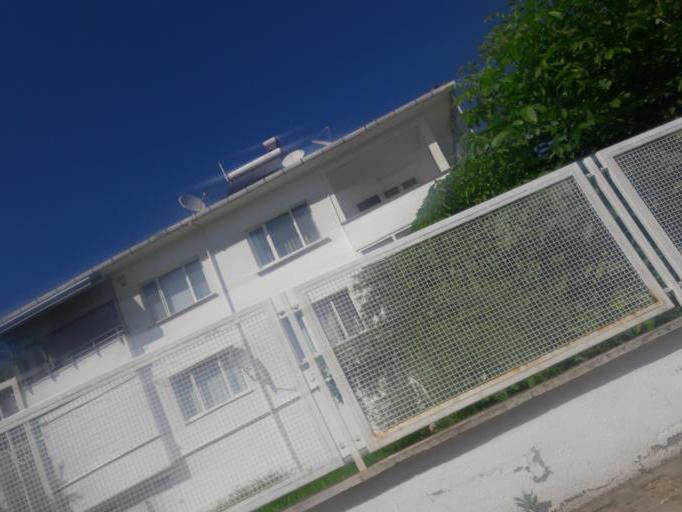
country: TR
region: Kocaeli
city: Kandira
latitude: 41.1583
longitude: 30.1952
